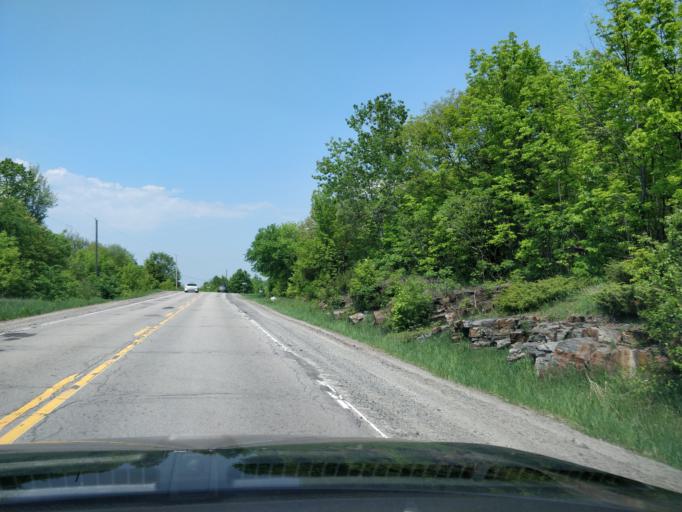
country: CA
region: Ontario
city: Perth
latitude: 44.7499
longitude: -76.3901
